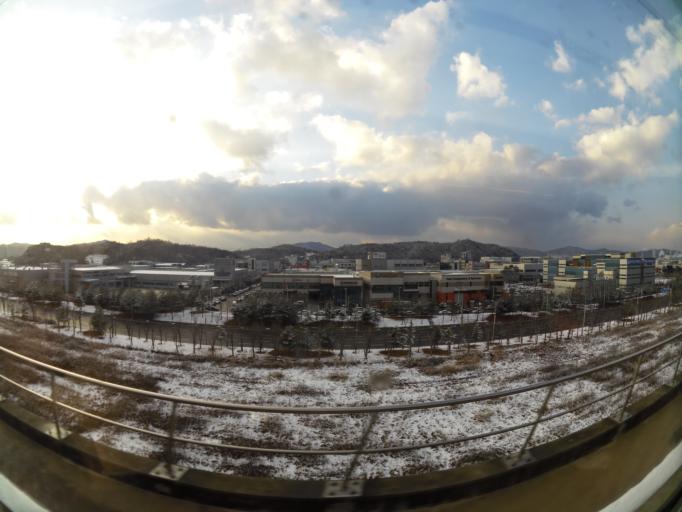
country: KR
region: Daejeon
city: Songgang-dong
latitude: 36.4135
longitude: 127.4154
